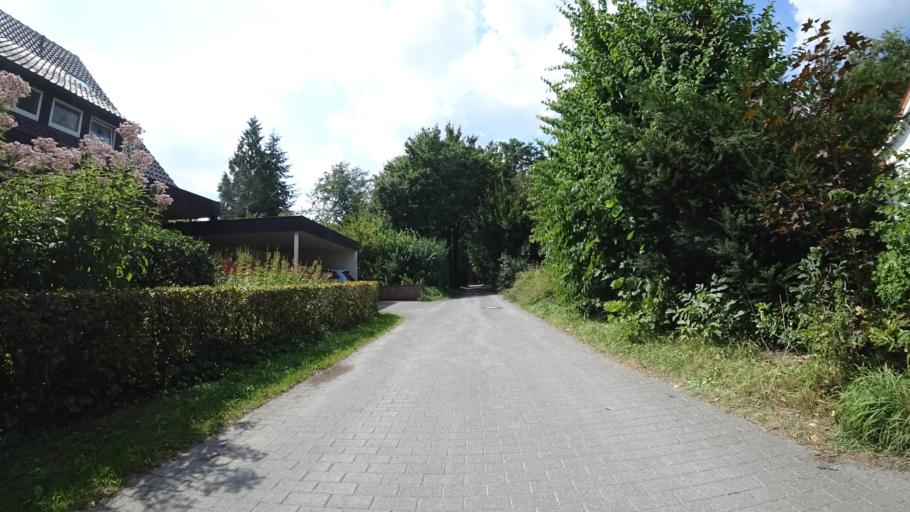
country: DE
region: North Rhine-Westphalia
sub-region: Regierungsbezirk Detmold
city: Guetersloh
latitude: 51.9195
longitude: 8.4257
